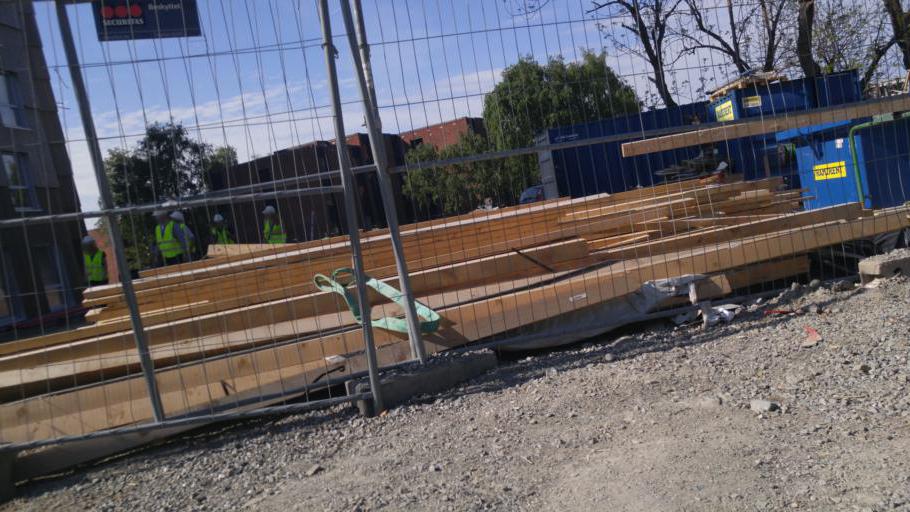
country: NO
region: Sor-Trondelag
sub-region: Trondheim
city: Trondheim
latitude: 63.4113
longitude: 10.4342
